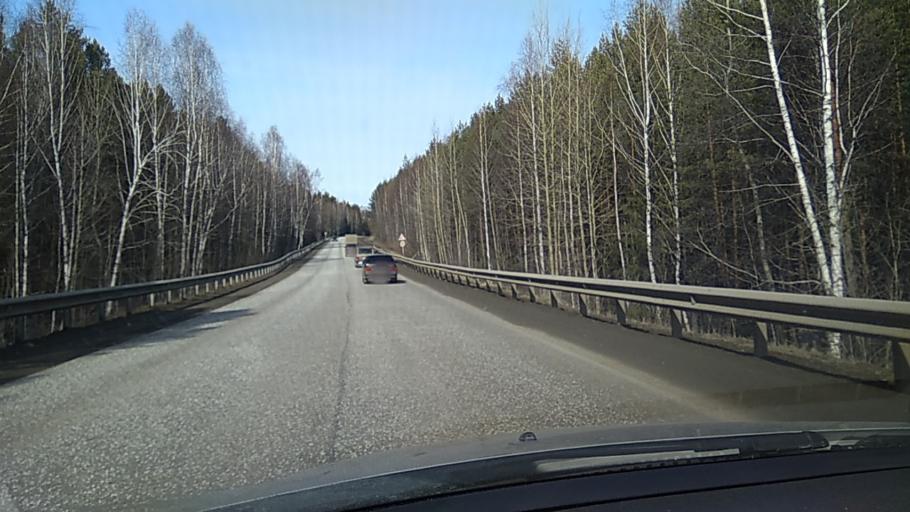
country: RU
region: Sverdlovsk
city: Chernoistochinsk
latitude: 57.7710
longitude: 59.8906
